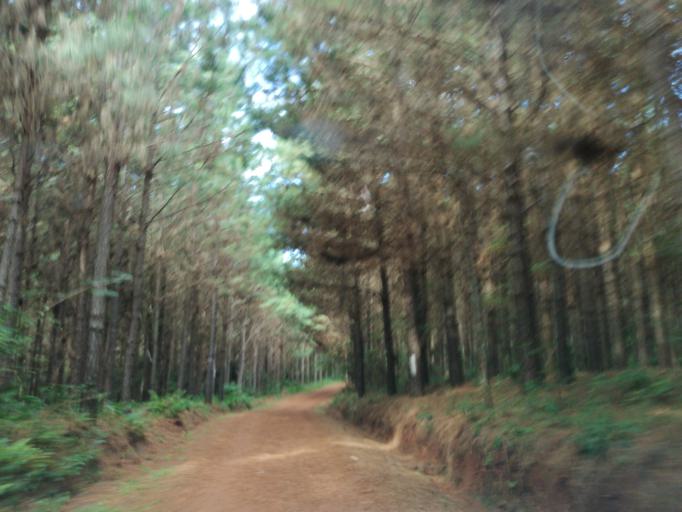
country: AR
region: Misiones
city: Dos de Mayo
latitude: -27.0162
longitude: -54.4191
